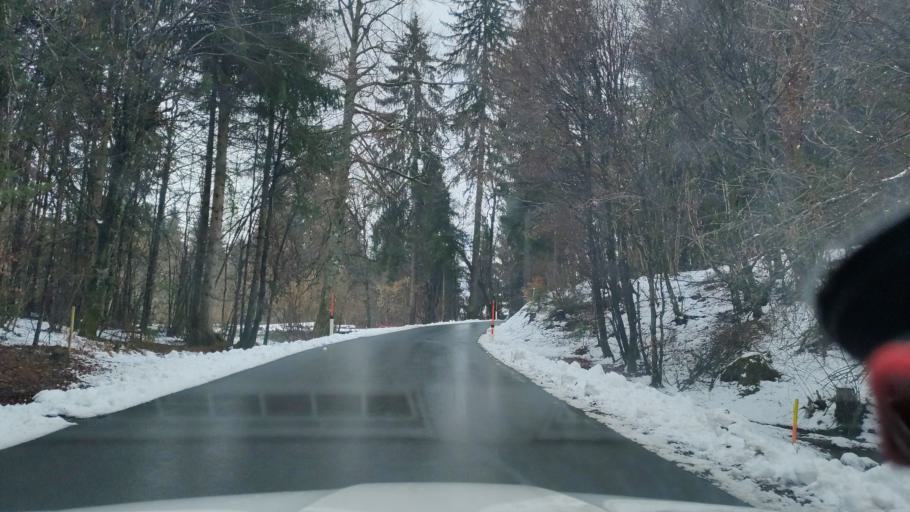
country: AT
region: Carinthia
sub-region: Politischer Bezirk Hermagor
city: Hermagor
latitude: 46.6260
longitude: 13.3532
